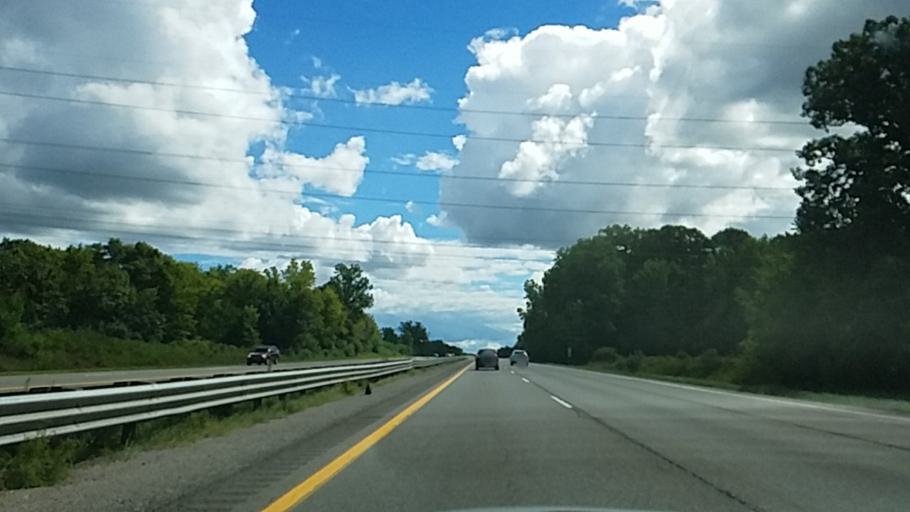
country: US
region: Michigan
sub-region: Washtenaw County
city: Ann Arbor
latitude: 42.3516
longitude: -83.7473
